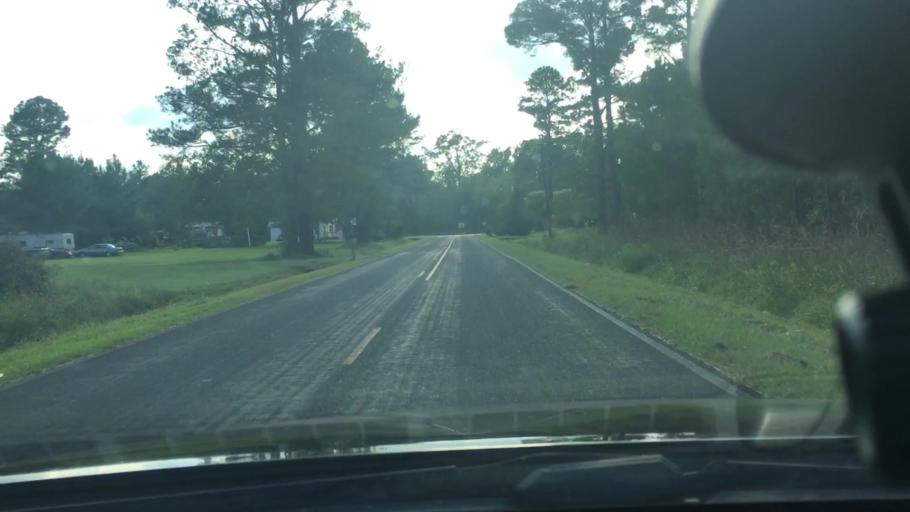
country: US
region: North Carolina
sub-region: Craven County
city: Vanceboro
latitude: 35.3331
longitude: -77.1701
